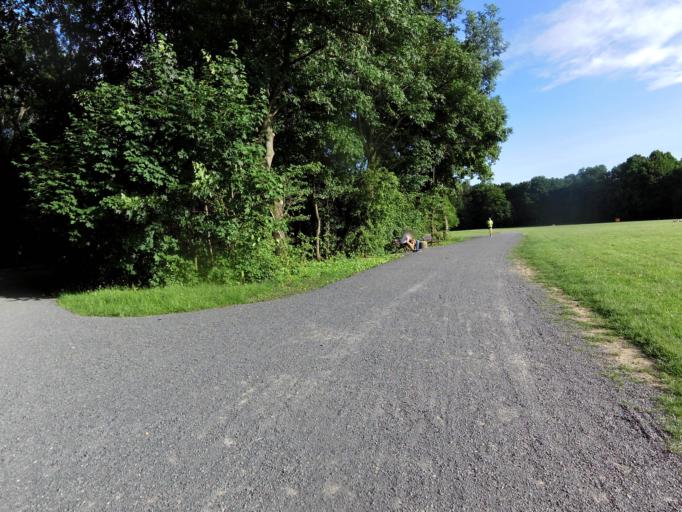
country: DE
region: Saxony
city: Leipzig
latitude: 51.3497
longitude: 12.3660
